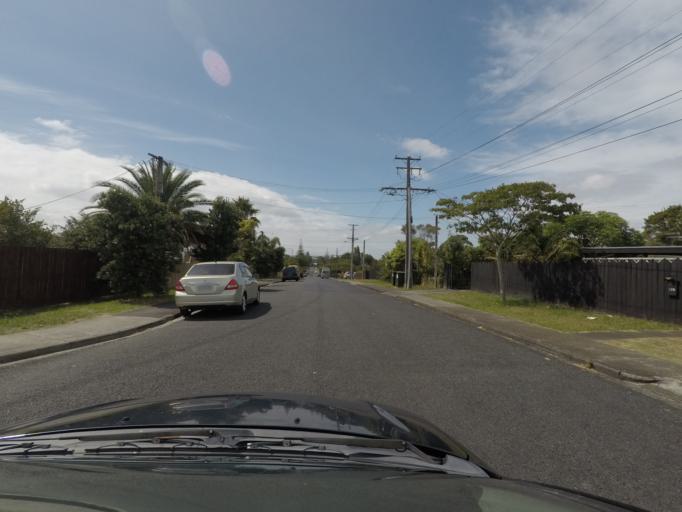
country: NZ
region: Auckland
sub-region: Auckland
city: Rosebank
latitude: -36.8942
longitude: 174.6665
